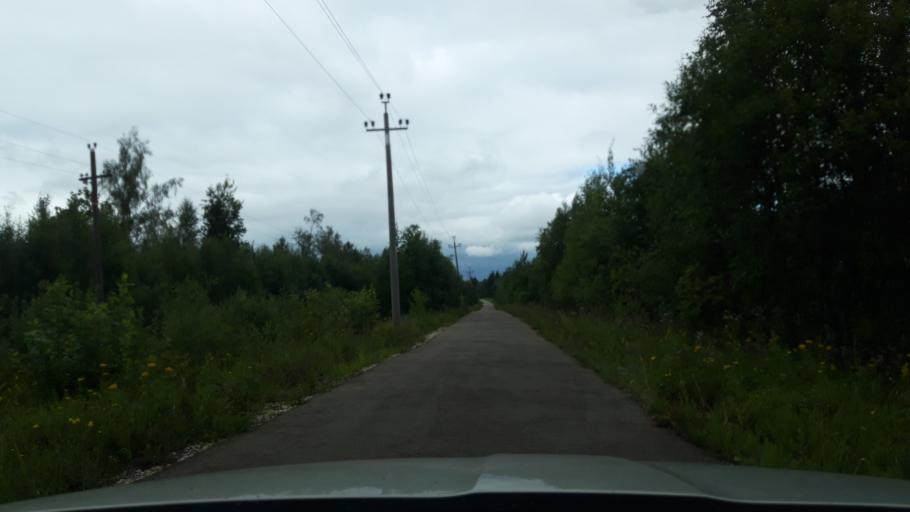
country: RU
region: Moskovskaya
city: Povarovo
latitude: 56.0405
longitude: 37.0540
